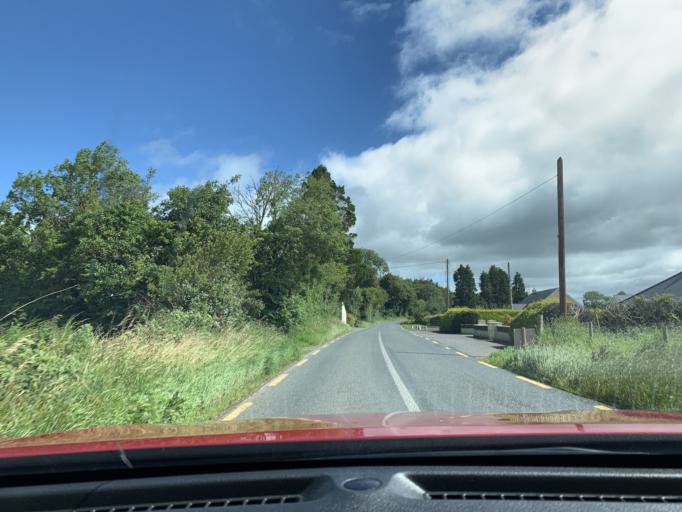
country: IE
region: Connaught
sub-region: Roscommon
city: Boyle
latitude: 53.8400
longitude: -8.2170
